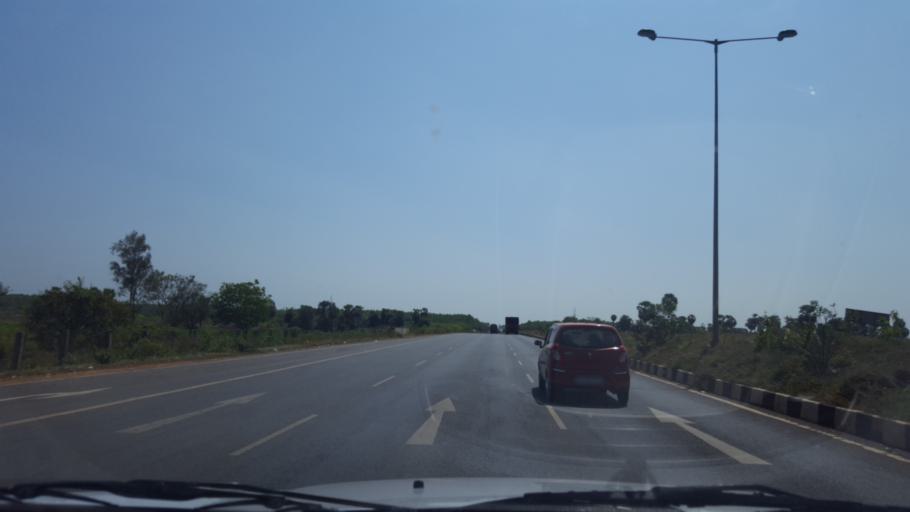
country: IN
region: Andhra Pradesh
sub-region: Nellore
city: Kovur
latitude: 14.6764
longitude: 79.9746
